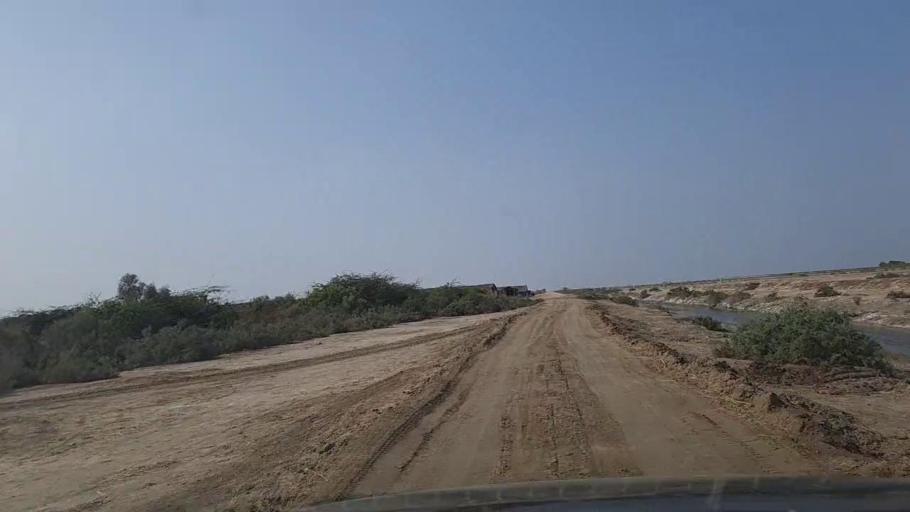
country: PK
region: Sindh
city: Gharo
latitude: 24.7074
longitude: 67.5429
